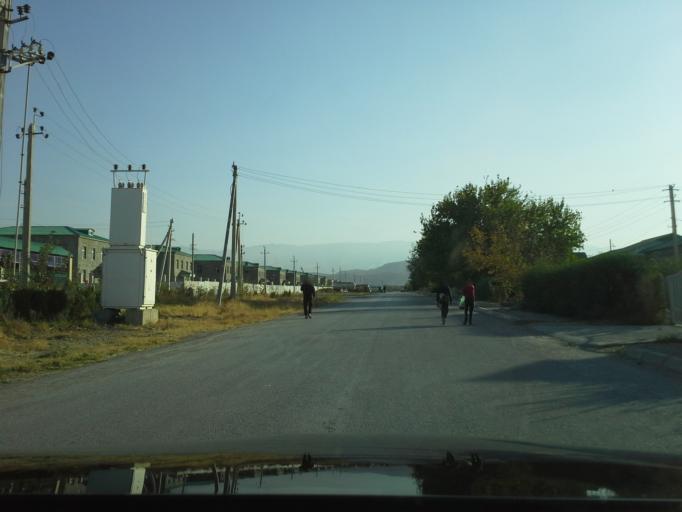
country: TM
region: Ahal
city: Abadan
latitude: 38.0482
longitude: 58.1692
